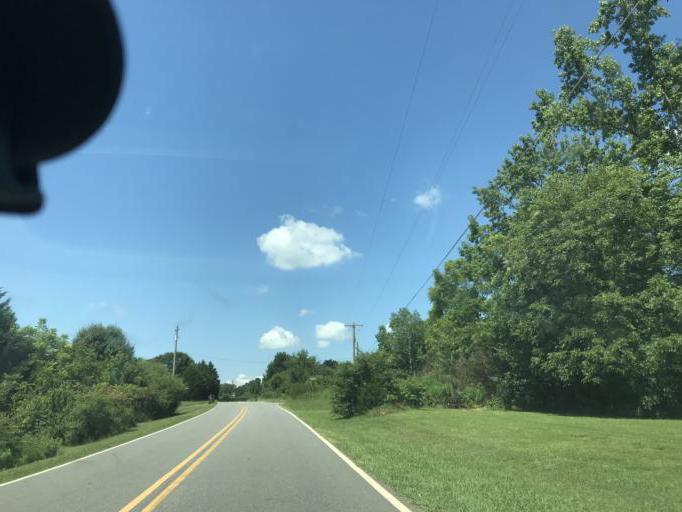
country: US
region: Georgia
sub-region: Dawson County
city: Dawsonville
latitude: 34.3193
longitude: -84.0072
